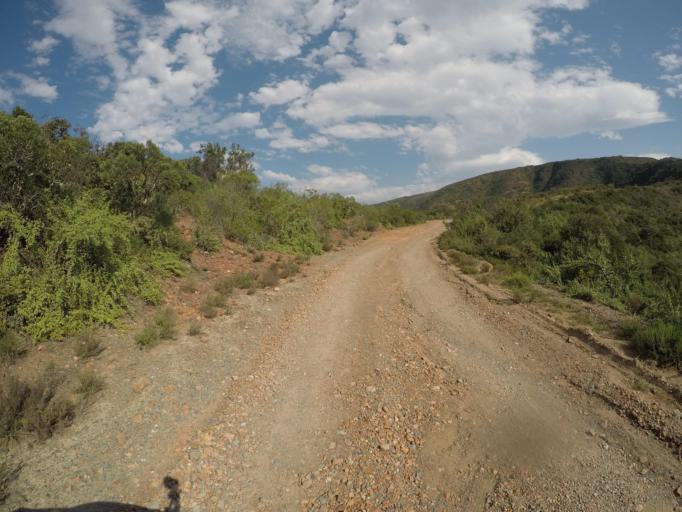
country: ZA
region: Eastern Cape
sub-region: Cacadu District Municipality
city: Kareedouw
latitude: -33.6492
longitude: 24.3500
